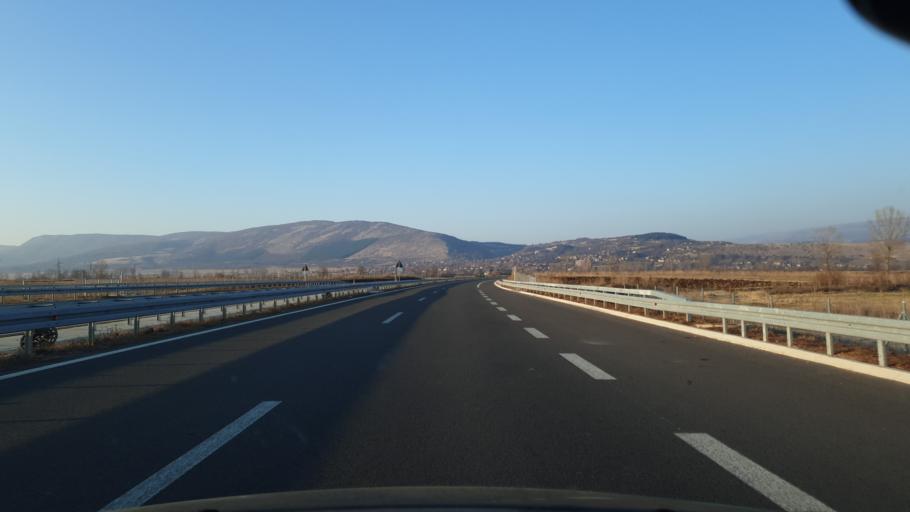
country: RS
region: Central Serbia
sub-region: Pirotski Okrug
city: Pirot
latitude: 43.1379
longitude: 22.5693
